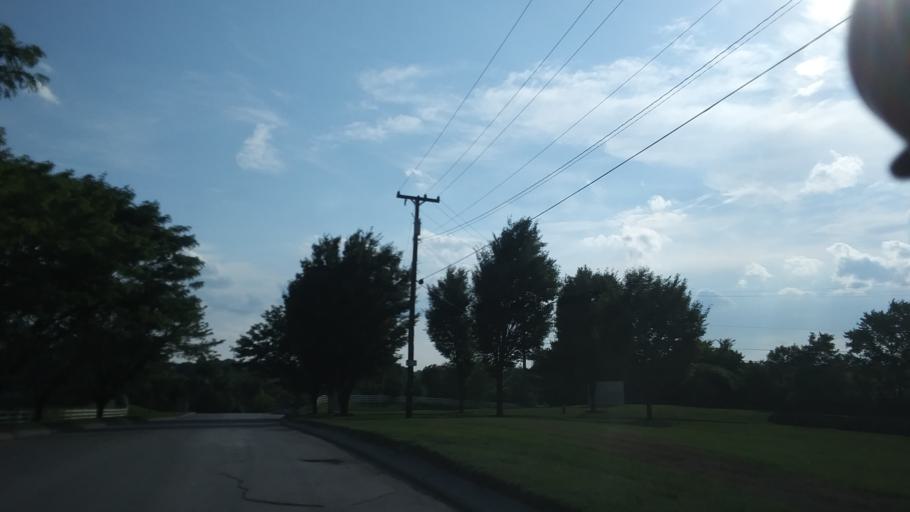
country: US
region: Tennessee
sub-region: Davidson County
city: Oak Hill
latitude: 36.0821
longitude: -86.6777
